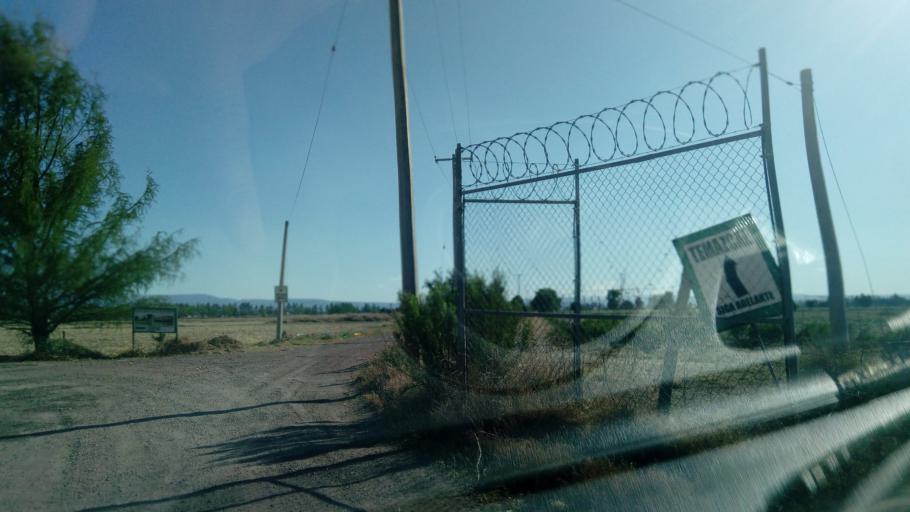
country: MX
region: Durango
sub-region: Durango
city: Jose Refugio Salcido
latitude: 24.0134
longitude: -104.5545
